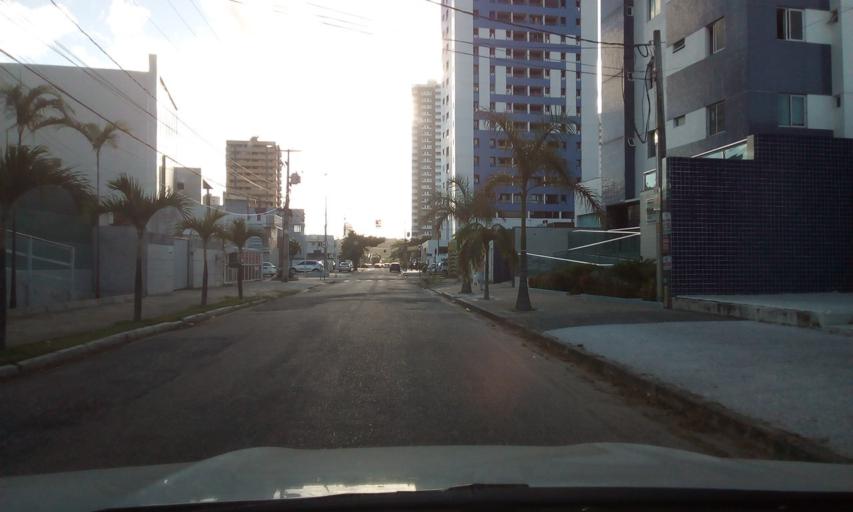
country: BR
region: Paraiba
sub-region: Joao Pessoa
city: Joao Pessoa
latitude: -7.1019
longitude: -34.8356
